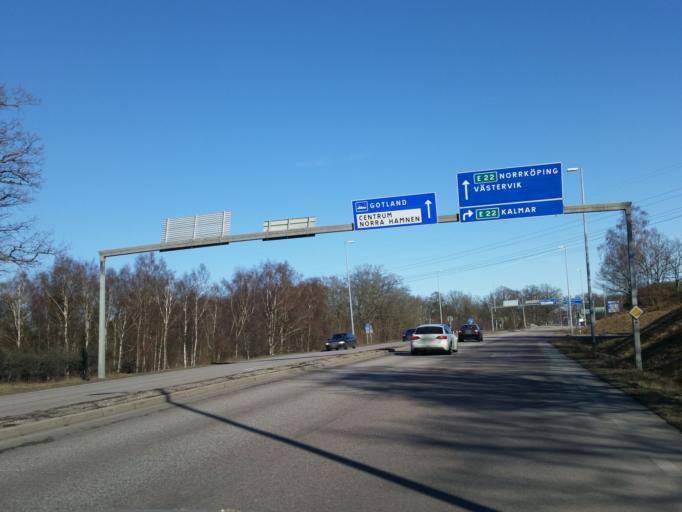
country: SE
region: Kalmar
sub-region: Oskarshamns Kommun
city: Oskarshamn
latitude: 57.2648
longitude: 16.4241
